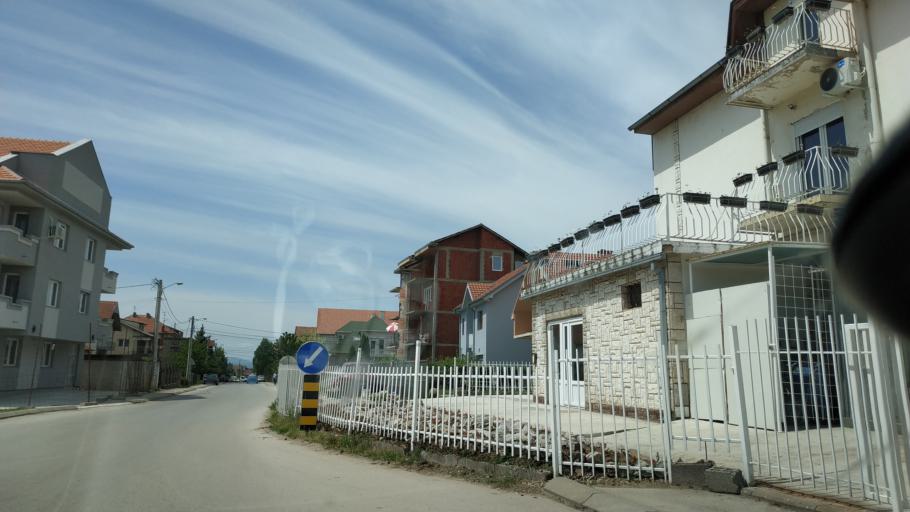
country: RS
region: Central Serbia
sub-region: Nisavski Okrug
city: Nis
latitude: 43.3373
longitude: 21.9170
